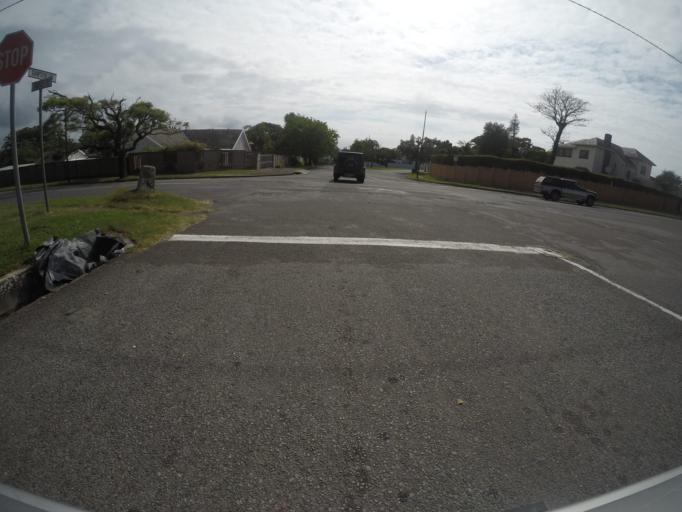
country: ZA
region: Eastern Cape
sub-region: Buffalo City Metropolitan Municipality
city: East London
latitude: -32.9927
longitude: 27.9011
